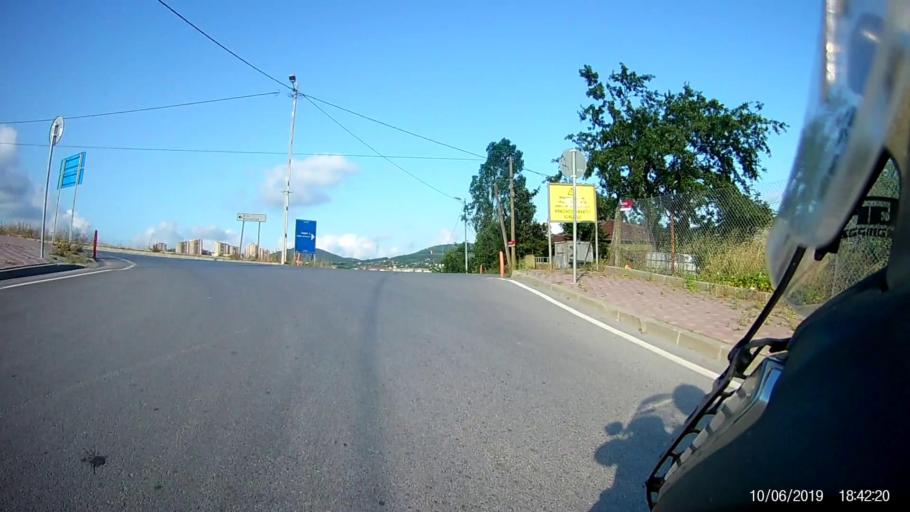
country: TR
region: Istanbul
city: Sancaktepe
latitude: 41.0361
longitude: 29.2586
